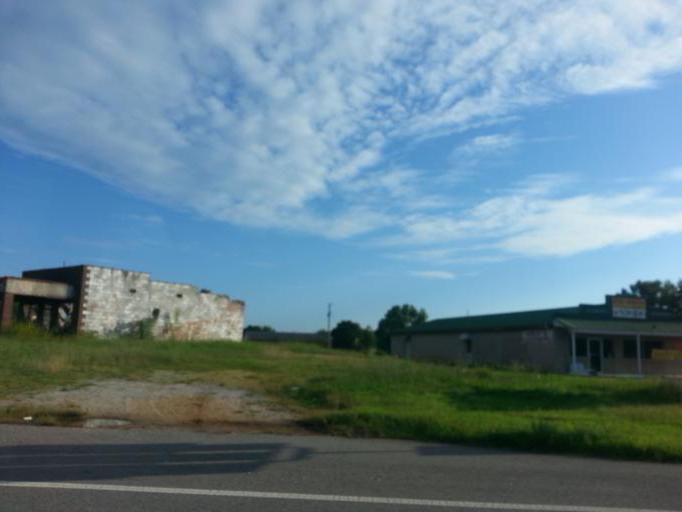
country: US
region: Alabama
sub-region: Lauderdale County
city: Rogersville
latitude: 34.8489
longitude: -87.3915
